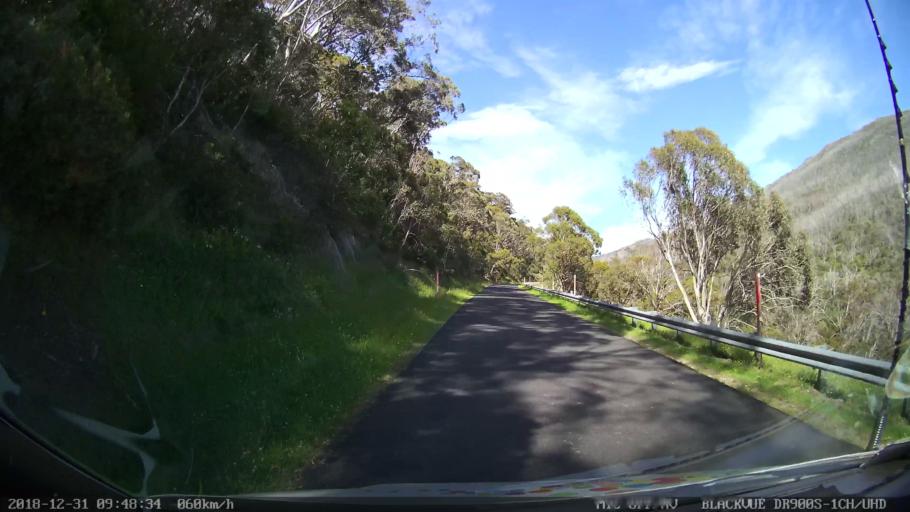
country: AU
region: New South Wales
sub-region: Snowy River
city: Jindabyne
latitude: -36.5134
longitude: 148.2912
